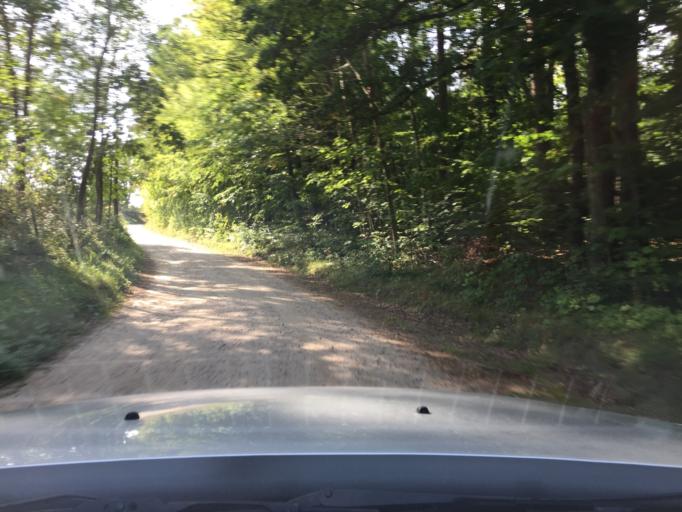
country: SE
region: Skane
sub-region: Kristianstads Kommun
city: Degeberga
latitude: 55.7275
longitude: 14.1150
